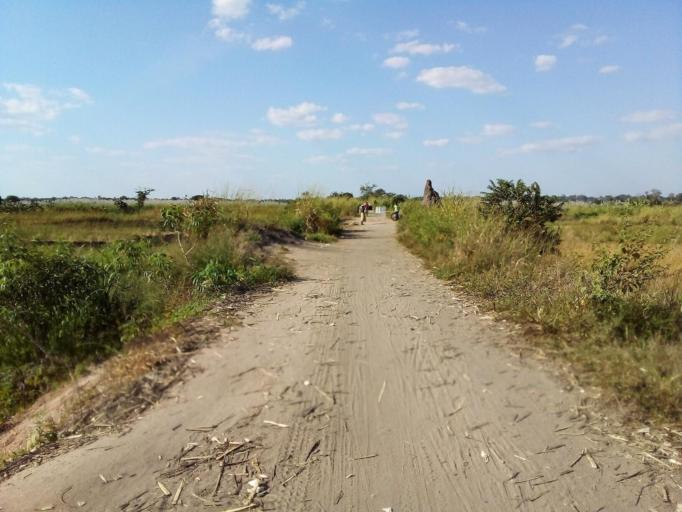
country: MZ
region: Zambezia
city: Quelimane
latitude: -17.5850
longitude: 36.8419
